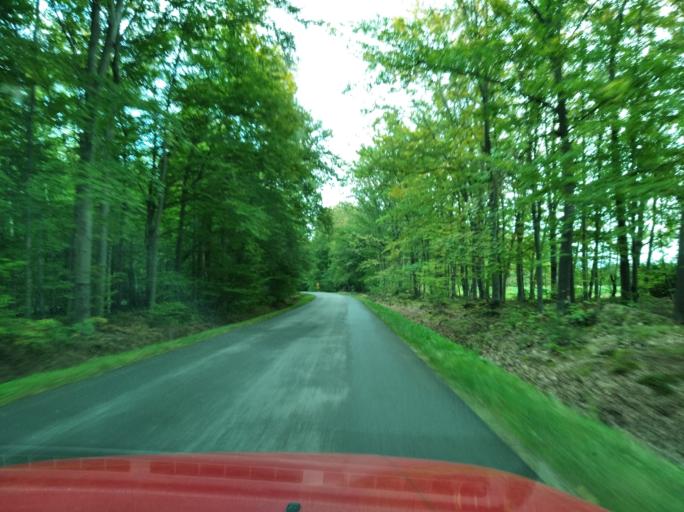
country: PL
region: Subcarpathian Voivodeship
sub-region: Powiat rzeszowski
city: Straszydle
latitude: 49.9308
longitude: 22.0024
